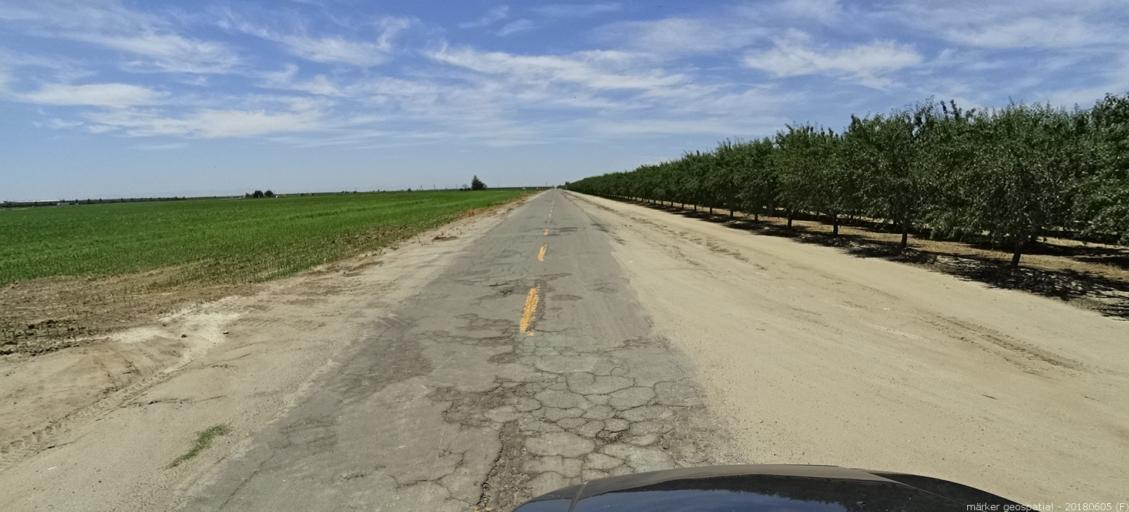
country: US
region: California
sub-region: Madera County
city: Chowchilla
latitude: 37.0906
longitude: -120.3742
